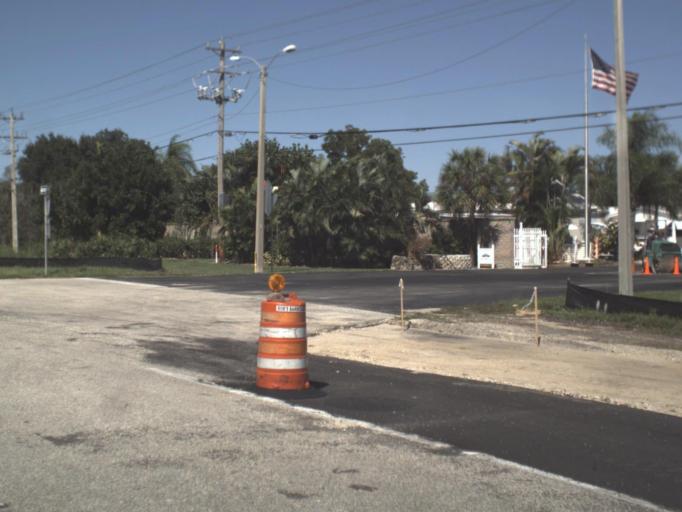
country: US
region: Florida
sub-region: Lee County
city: Suncoast Estates
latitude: 26.7433
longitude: -81.9165
